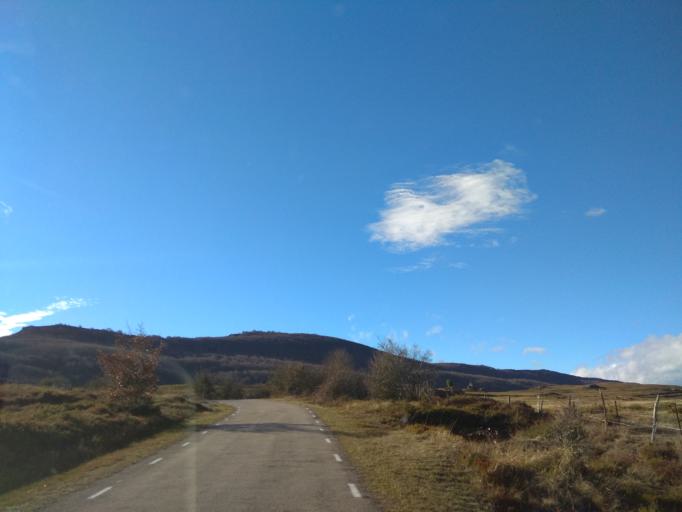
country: ES
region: Cantabria
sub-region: Provincia de Cantabria
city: San Martin de Elines
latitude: 42.9461
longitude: -3.8217
